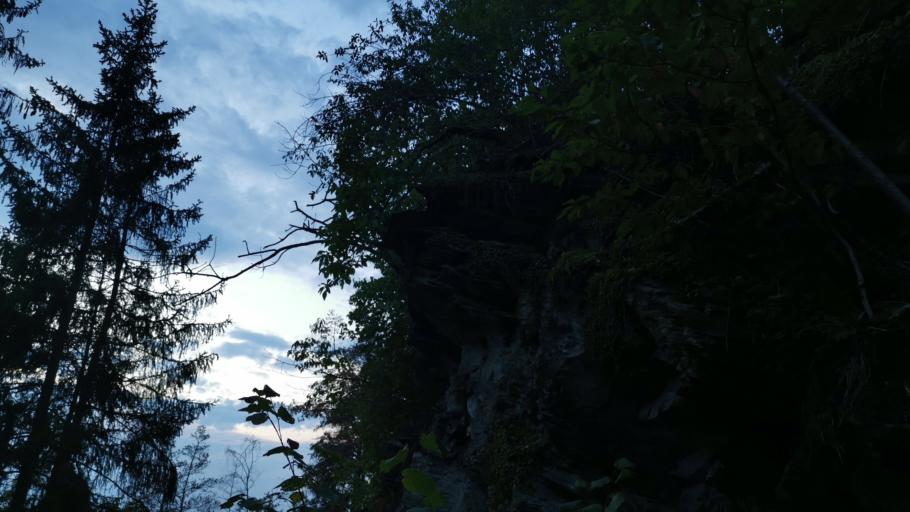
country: DE
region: Bavaria
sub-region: Upper Franconia
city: Topen
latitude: 50.3845
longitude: 11.8458
